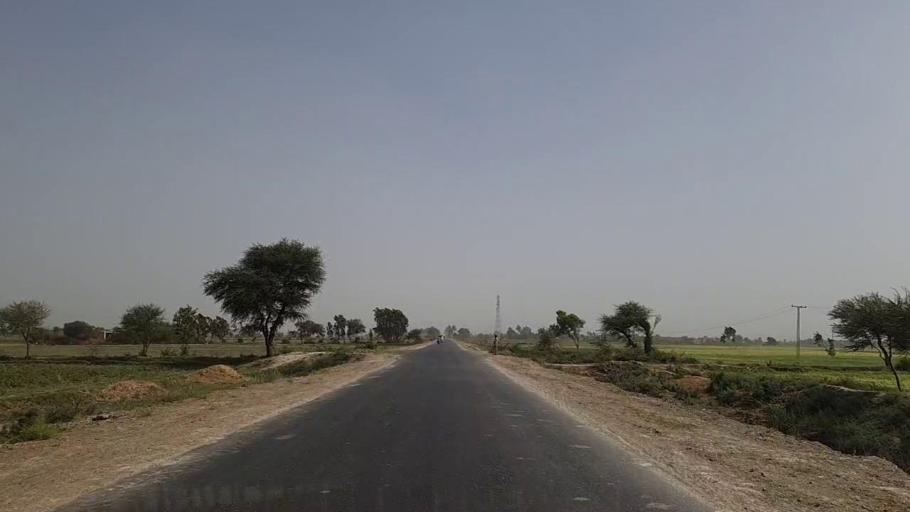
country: PK
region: Sindh
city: Tando Bago
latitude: 24.8204
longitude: 68.9034
